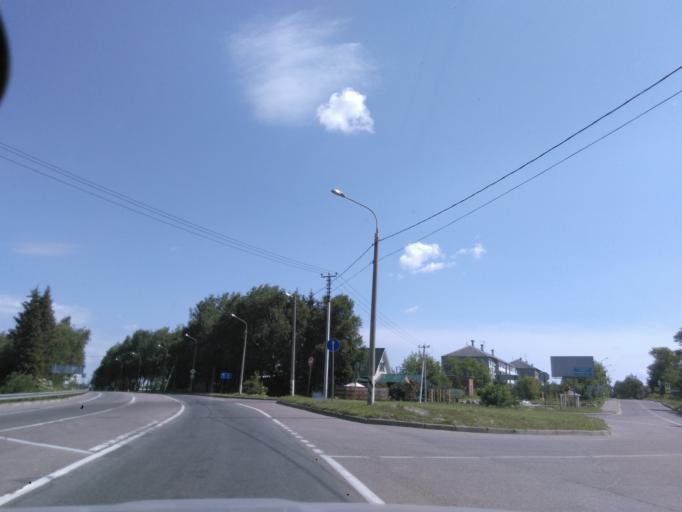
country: RU
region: Moskovskaya
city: Solnechnogorsk
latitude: 56.1819
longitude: 36.9592
